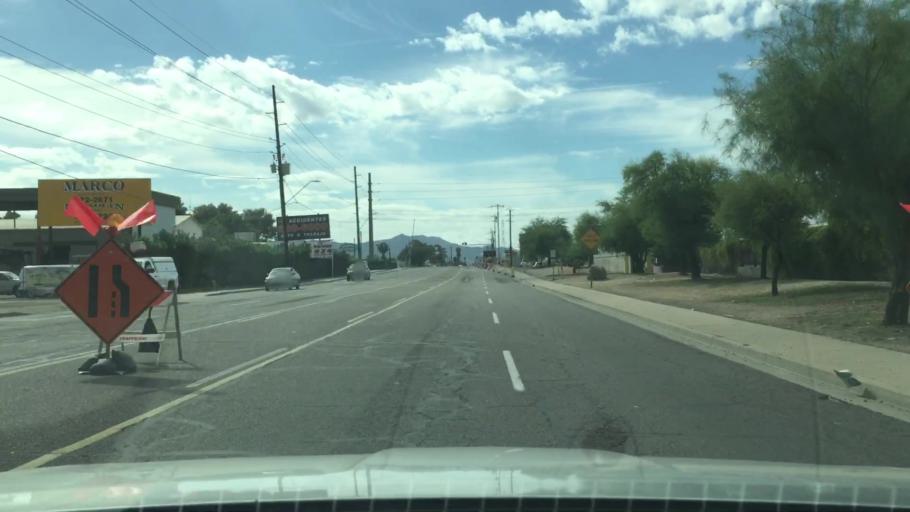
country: US
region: Arizona
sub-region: Maricopa County
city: Phoenix
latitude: 33.4463
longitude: -112.1345
